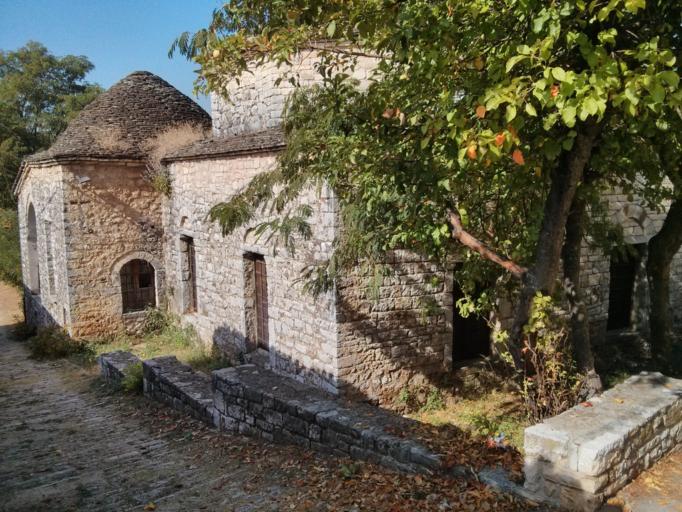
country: GR
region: Epirus
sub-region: Nomos Ioanninon
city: Ioannina
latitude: 39.6730
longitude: 20.8601
